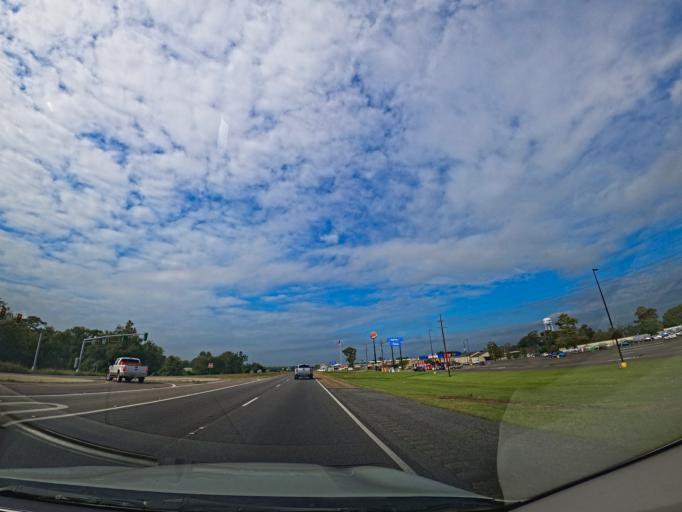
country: US
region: Louisiana
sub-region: Saint Mary Parish
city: Bayou Vista
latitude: 29.6817
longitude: -91.2670
